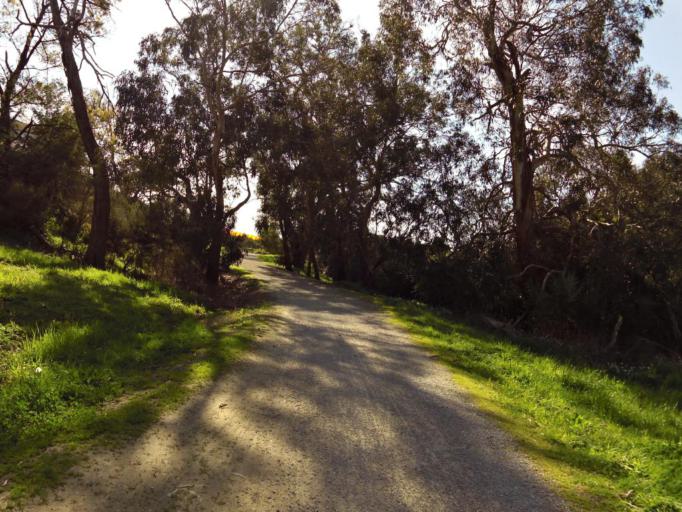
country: AU
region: Victoria
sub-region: Monash
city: Mulgrave
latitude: -37.9351
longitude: 145.2106
